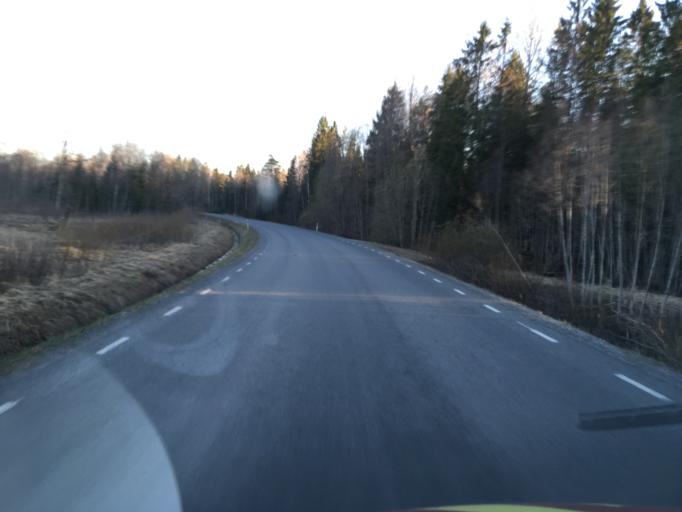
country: EE
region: Raplamaa
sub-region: Kehtna vald
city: Kehtna
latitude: 59.0315
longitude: 24.9225
